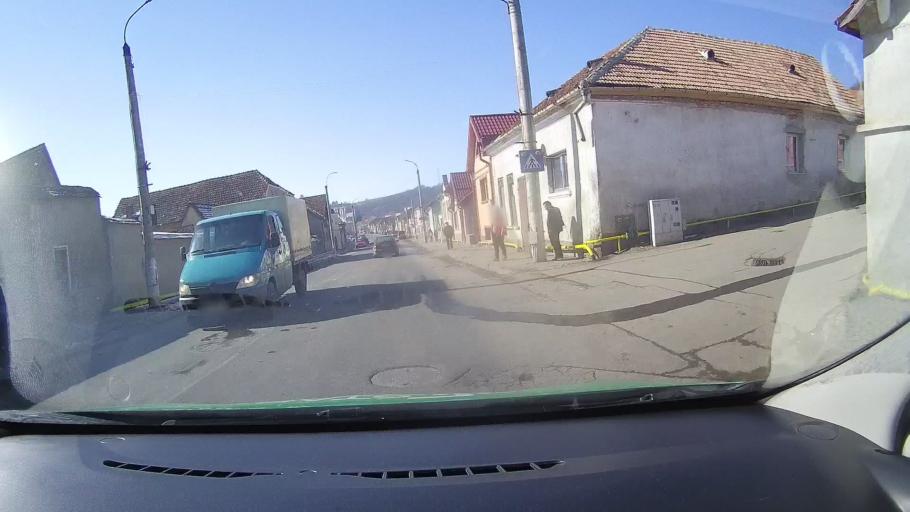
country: RO
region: Brasov
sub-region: Oras Rupea
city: Rupea
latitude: 46.0398
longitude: 25.2310
